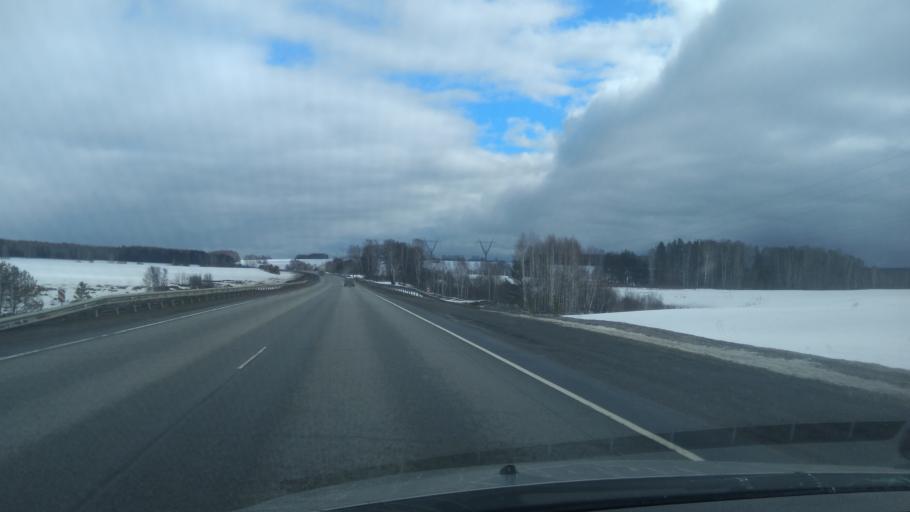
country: RU
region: Sverdlovsk
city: Ufimskiy
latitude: 56.7731
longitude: 58.0119
